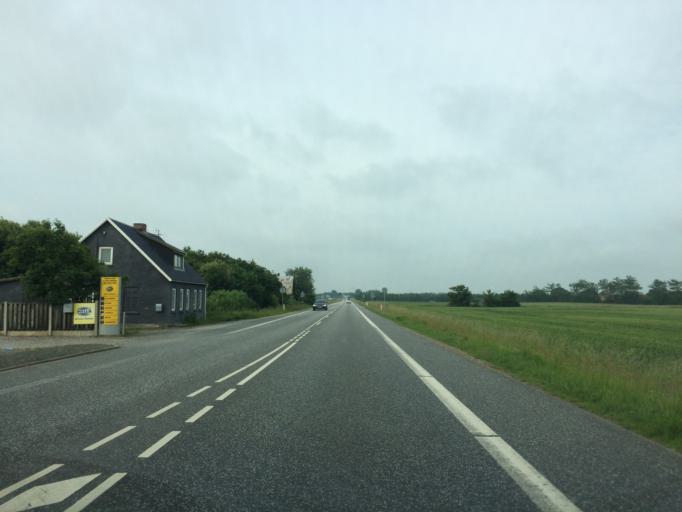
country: DK
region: Central Jutland
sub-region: Holstebro Kommune
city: Ulfborg
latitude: 56.2898
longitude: 8.3373
